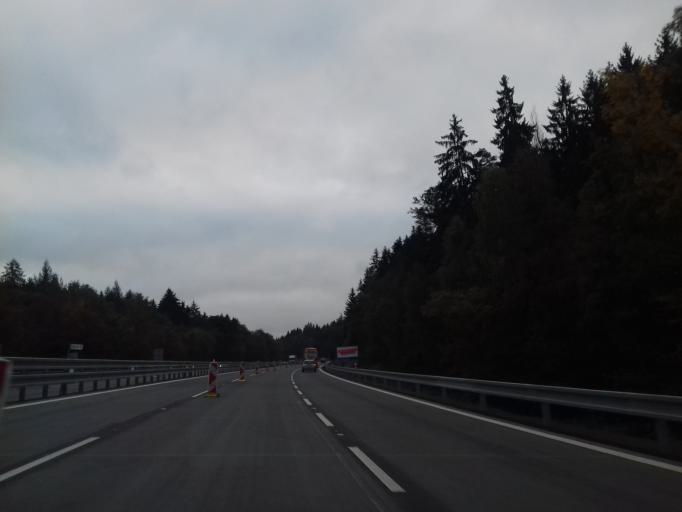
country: CZ
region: Central Bohemia
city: Ondrejov
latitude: 49.8535
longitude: 14.7970
